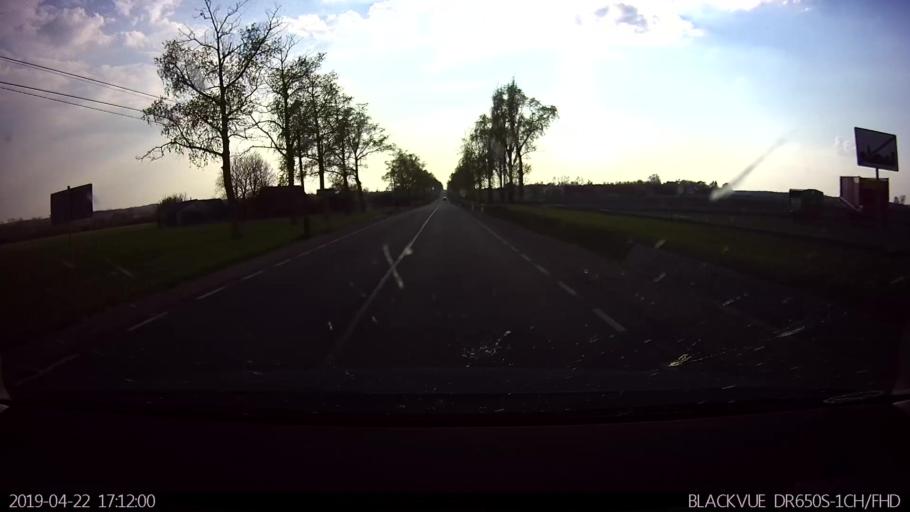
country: PL
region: Masovian Voivodeship
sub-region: Powiat siedlecki
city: Korczew
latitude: 52.4100
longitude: 22.5428
